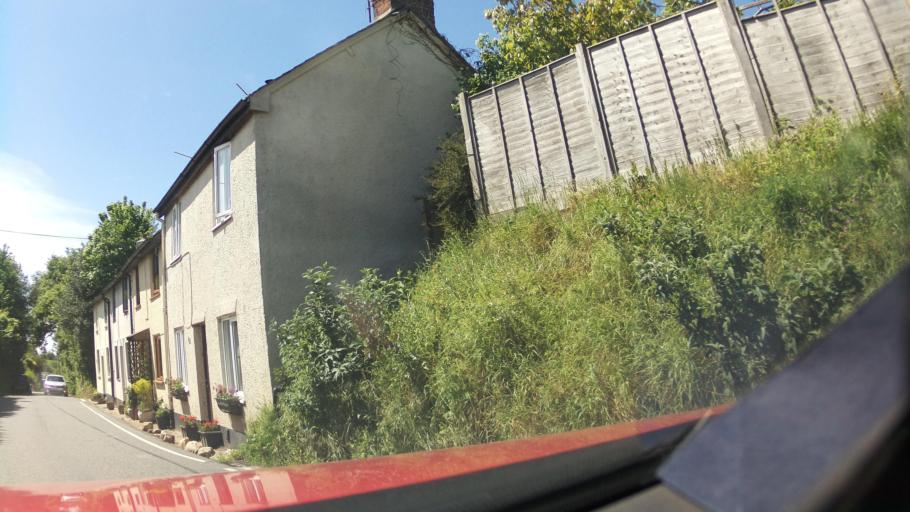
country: GB
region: England
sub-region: Devon
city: Ottery St Mary
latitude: 50.7750
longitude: -3.2561
